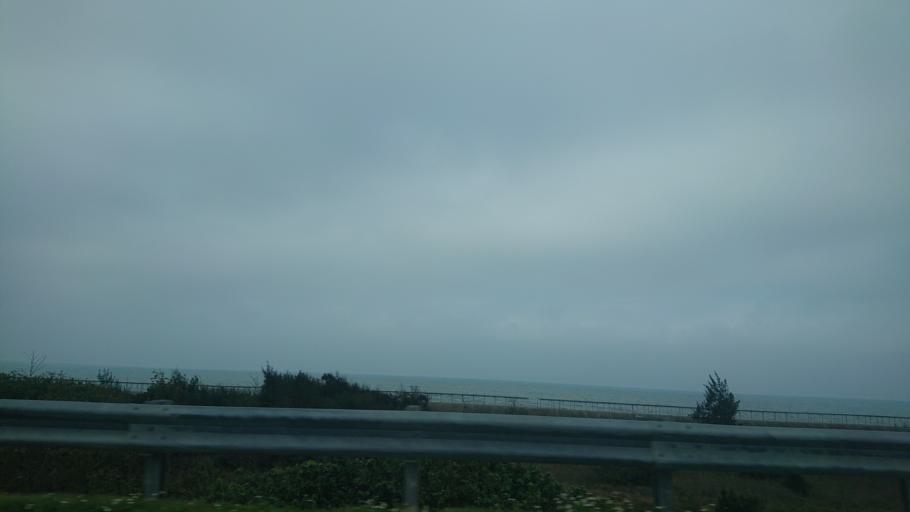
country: TW
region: Taiwan
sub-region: Miaoli
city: Miaoli
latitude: 24.5249
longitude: 120.6888
